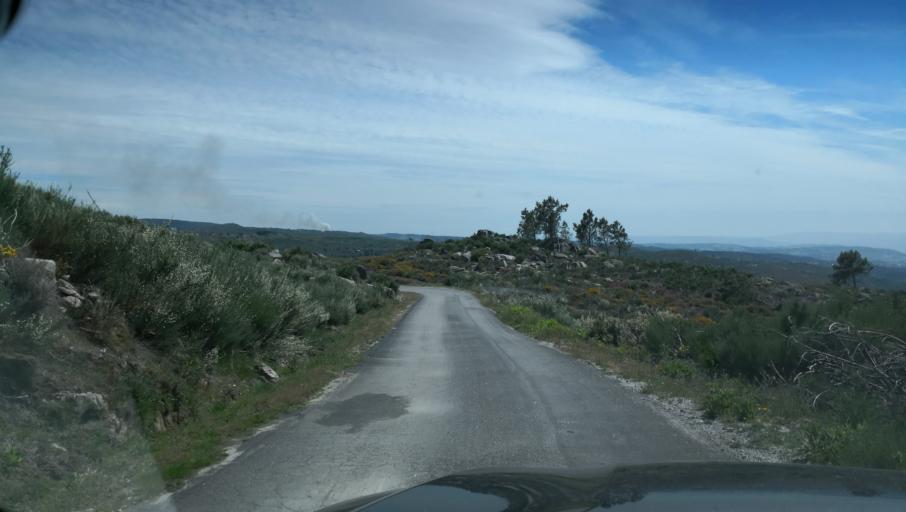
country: PT
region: Vila Real
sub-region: Vila Real
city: Vila Real
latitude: 41.3681
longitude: -7.6998
